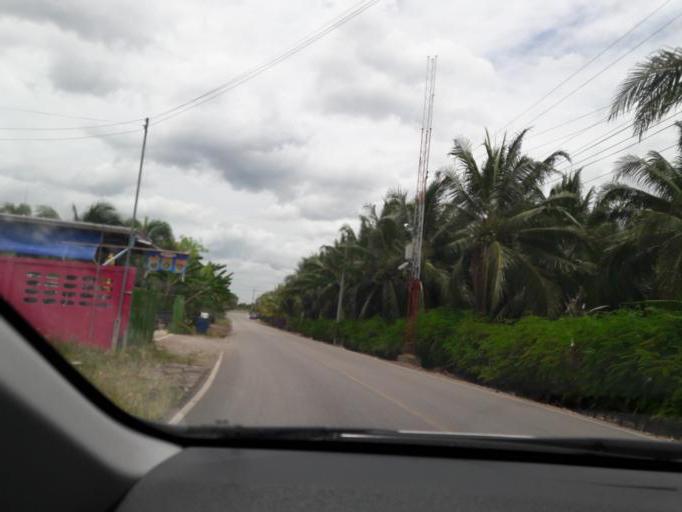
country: TH
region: Ratchaburi
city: Damnoen Saduak
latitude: 13.5462
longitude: 100.0116
